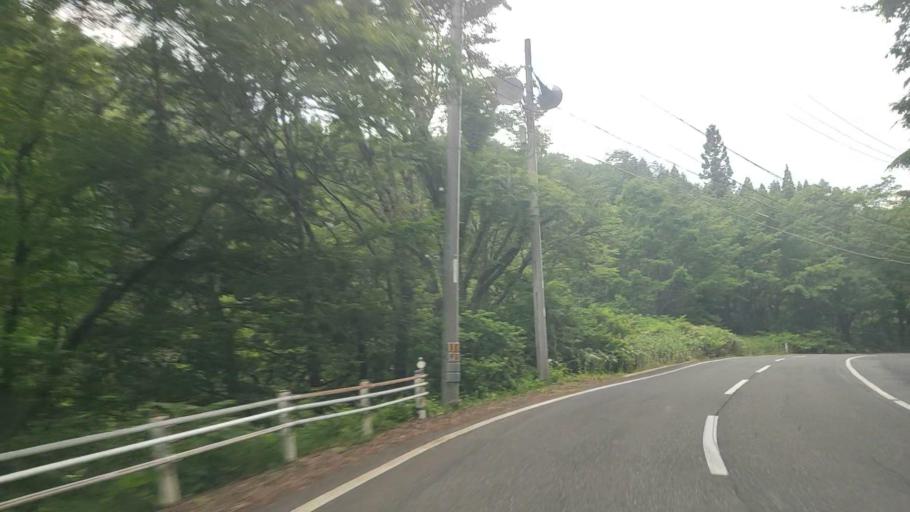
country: JP
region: Tottori
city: Kurayoshi
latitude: 35.2913
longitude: 133.9627
